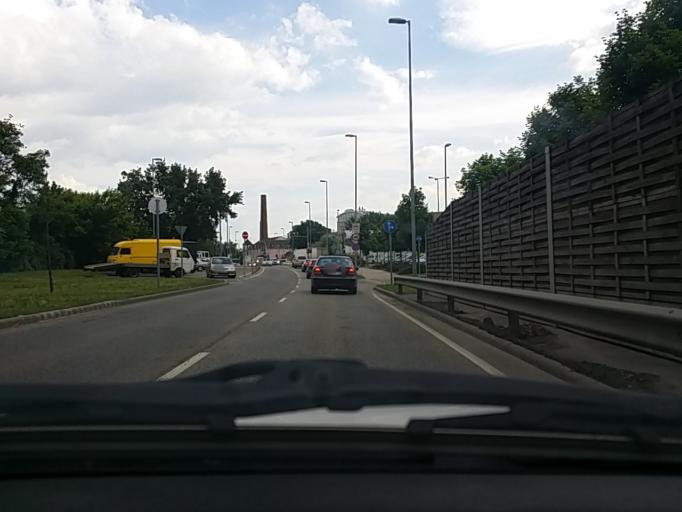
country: HU
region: Budapest
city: Budapest III. keruelet
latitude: 47.5537
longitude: 19.0486
